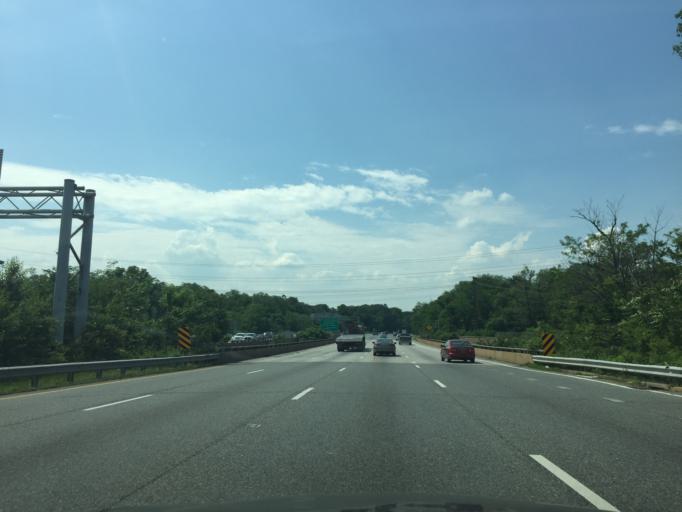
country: US
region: Maryland
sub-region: Anne Arundel County
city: Linthicum
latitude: 39.2099
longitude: -76.6481
